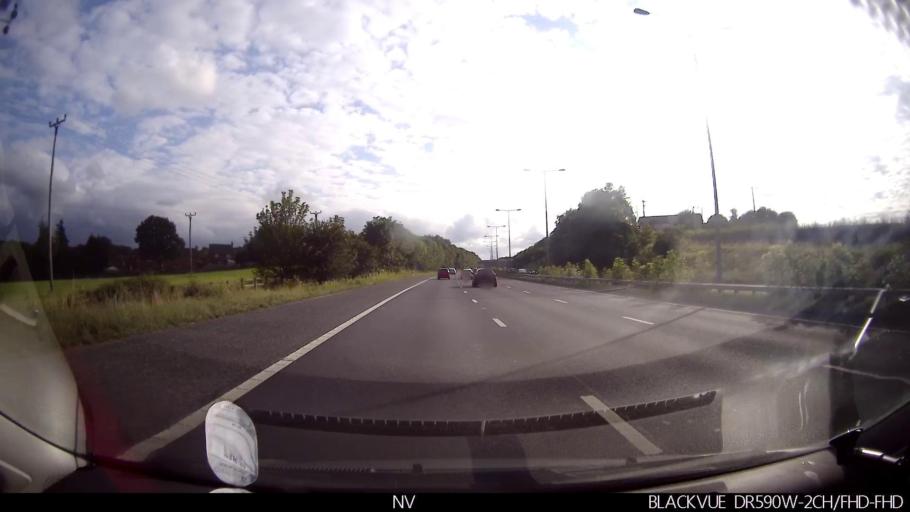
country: GB
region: England
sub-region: City and Borough of Leeds
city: Morley
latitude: 53.7616
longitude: -1.6002
